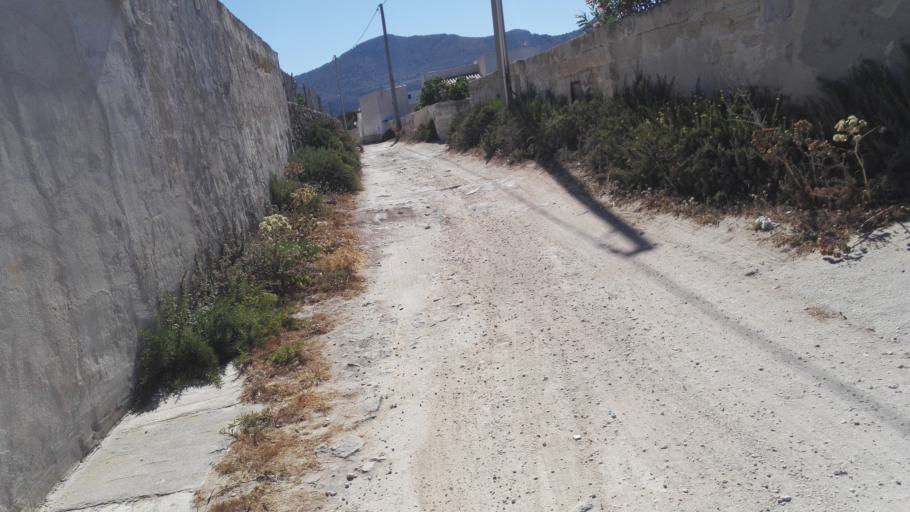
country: IT
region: Sicily
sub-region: Trapani
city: Favignana
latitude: 37.9354
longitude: 12.3402
